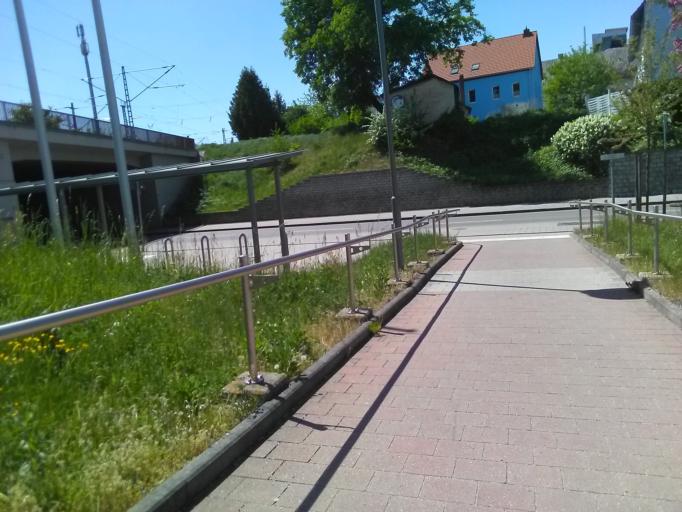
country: DE
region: Bavaria
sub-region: Regierungsbezirk Mittelfranken
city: Gunzenhausen
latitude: 49.1206
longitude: 10.7547
